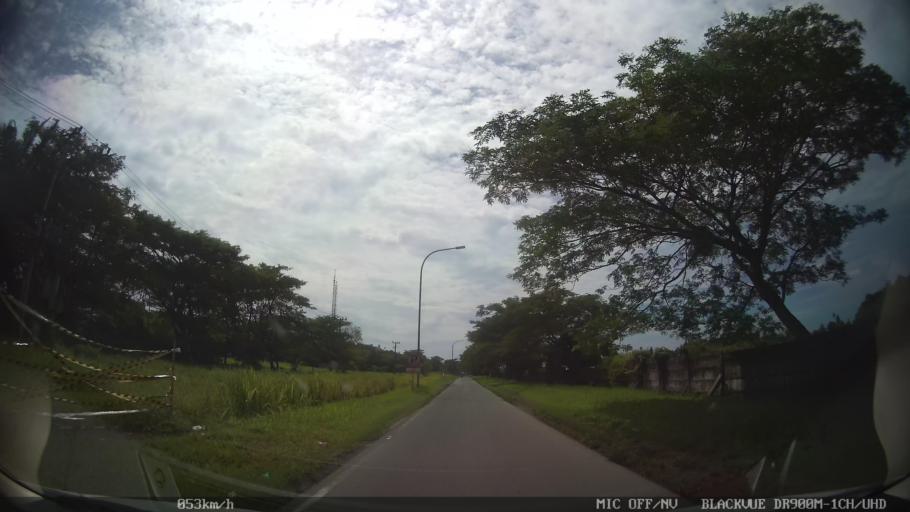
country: ID
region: North Sumatra
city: Percut
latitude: 3.6093
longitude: 98.8555
